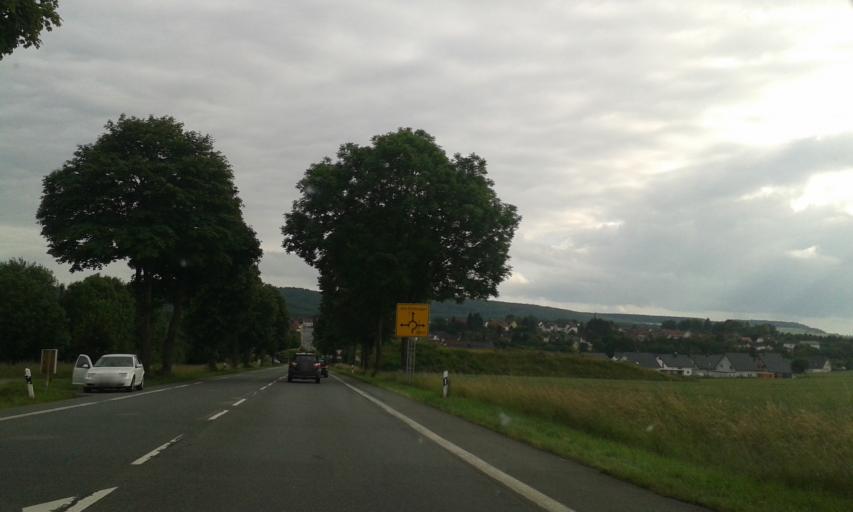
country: DE
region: North Rhine-Westphalia
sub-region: Regierungsbezirk Detmold
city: Barntrup
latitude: 52.0001
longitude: 9.1229
